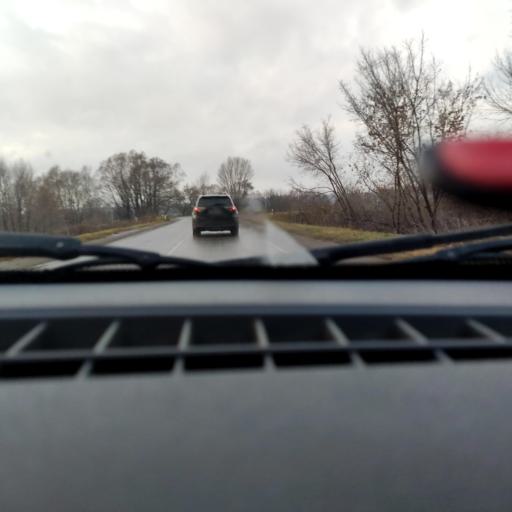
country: RU
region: Bashkortostan
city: Avdon
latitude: 54.5023
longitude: 55.8797
